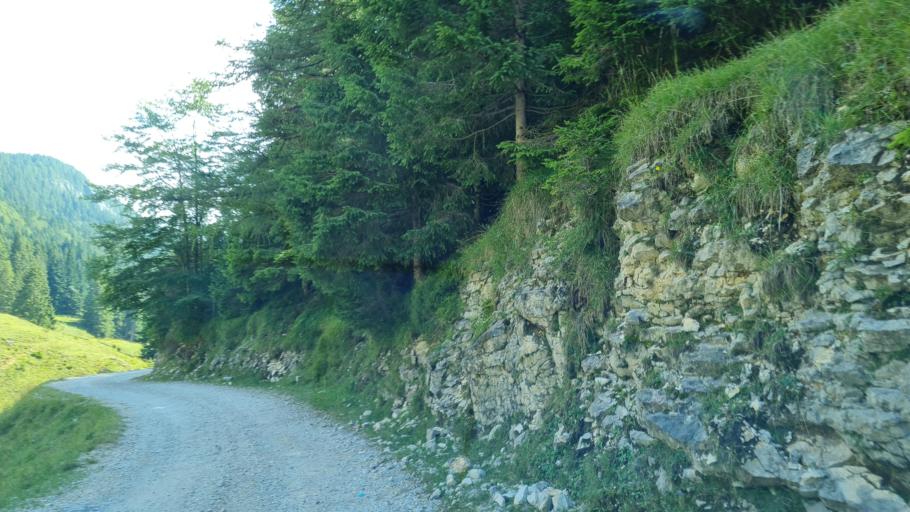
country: IT
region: Veneto
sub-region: Provincia di Vicenza
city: Asiago
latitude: 45.9367
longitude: 11.4928
